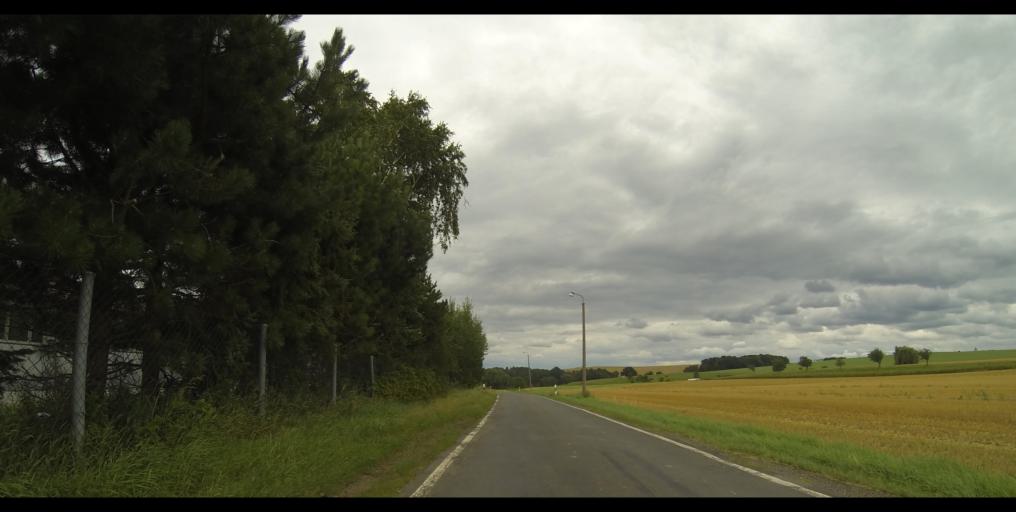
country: DE
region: Saxony
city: Reinsberg
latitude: 51.0226
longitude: 13.4109
